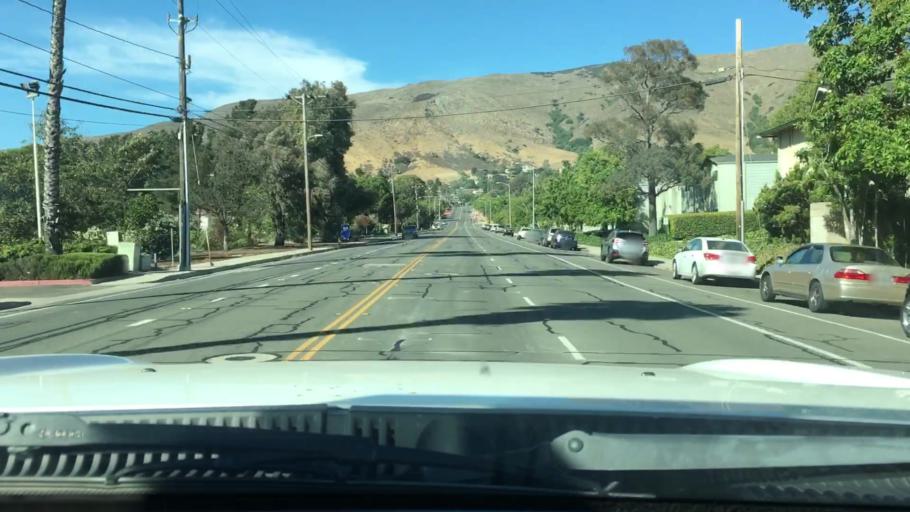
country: US
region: California
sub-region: San Luis Obispo County
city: San Luis Obispo
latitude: 35.2621
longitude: -120.6430
